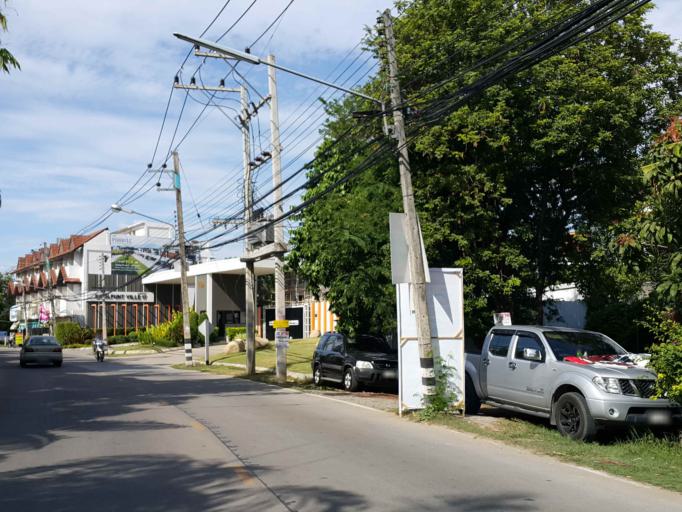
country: TH
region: Chiang Mai
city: Chiang Mai
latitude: 18.7580
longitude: 98.9951
